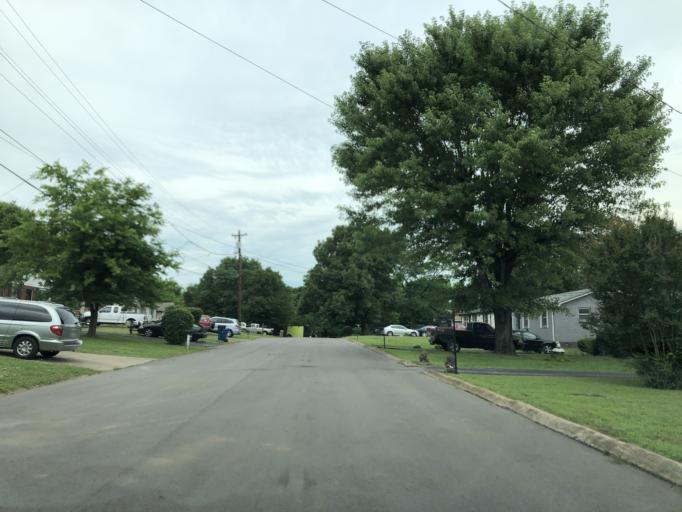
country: US
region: Tennessee
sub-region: Davidson County
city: Goodlettsville
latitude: 36.2826
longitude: -86.7033
